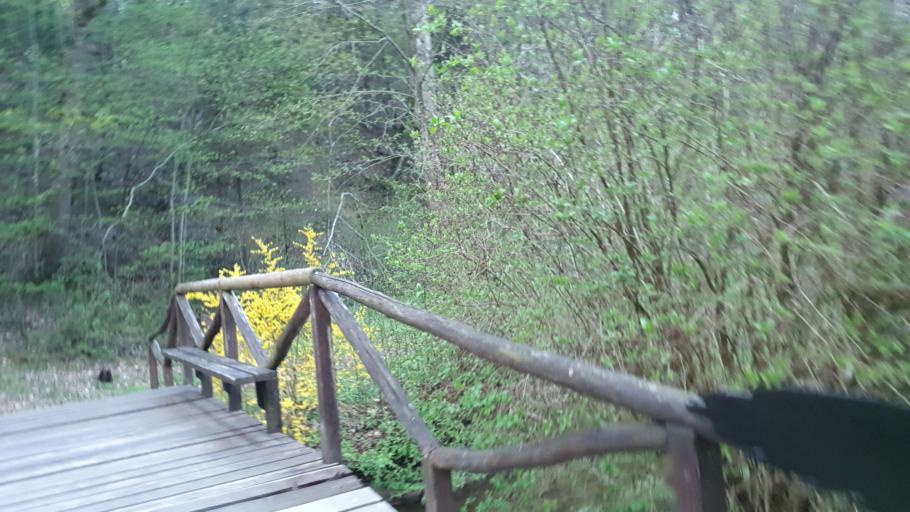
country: LT
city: Sakiai
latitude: 55.0800
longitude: 23.1784
